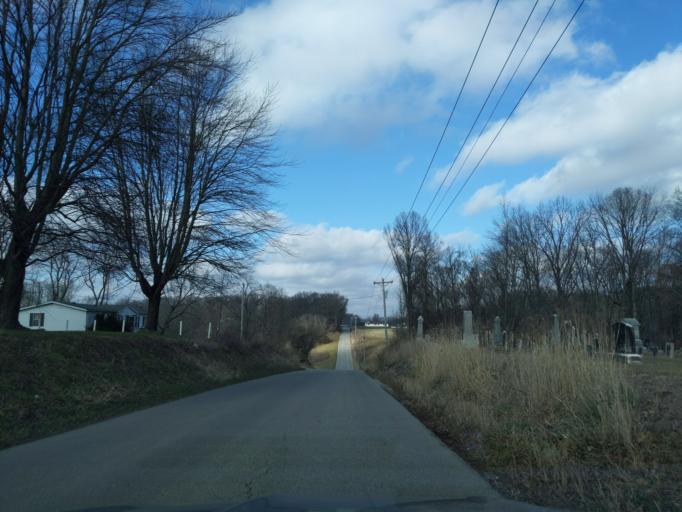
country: US
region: Indiana
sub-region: Ripley County
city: Batesville
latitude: 39.3241
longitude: -85.3258
